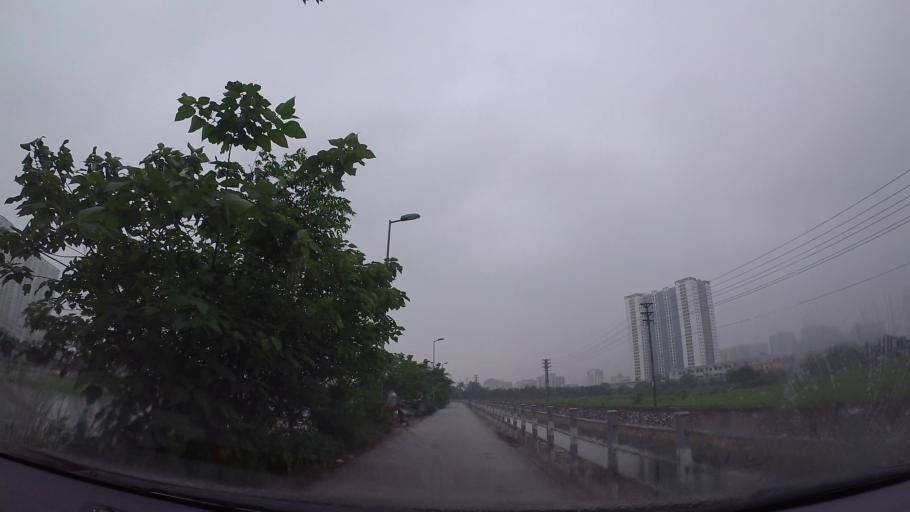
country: VN
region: Ha Noi
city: Van Dien
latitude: 20.9786
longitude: 105.8733
